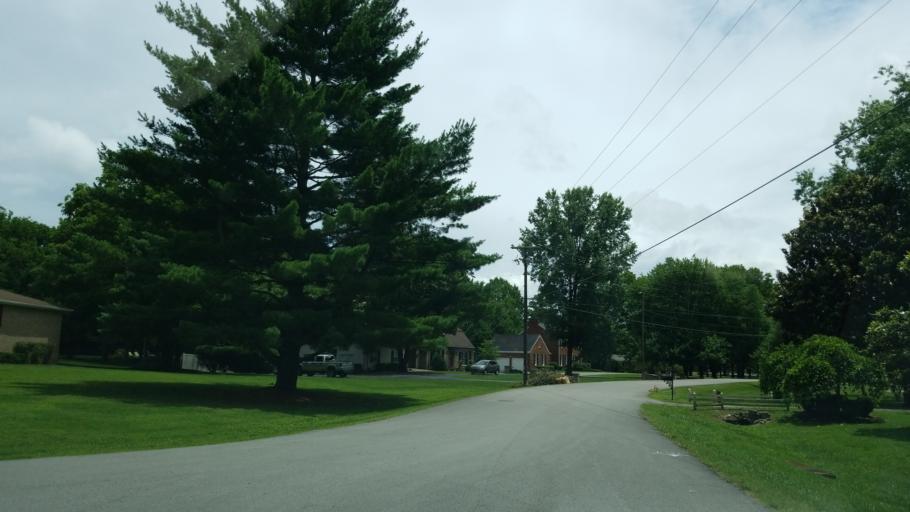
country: US
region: Tennessee
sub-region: Davidson County
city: Forest Hills
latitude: 36.0357
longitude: -86.8349
